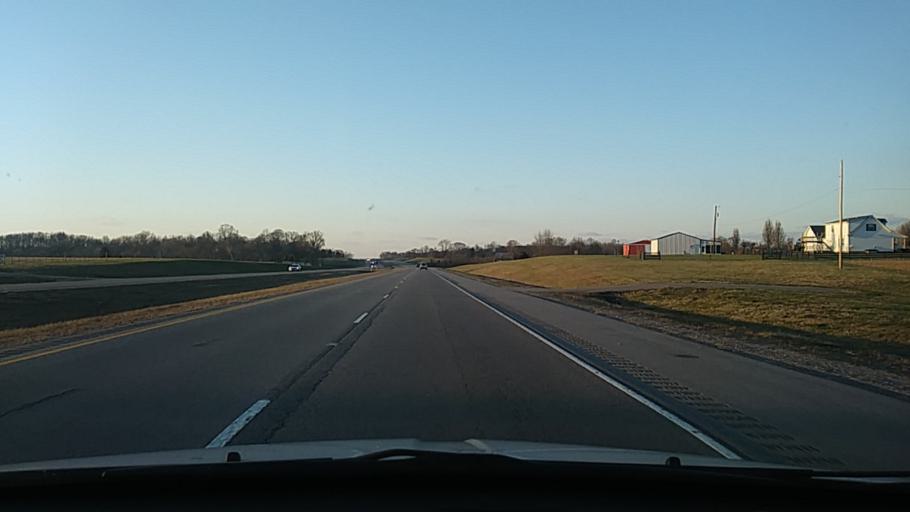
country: US
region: Tennessee
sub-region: Sumner County
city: Portland
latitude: 36.5002
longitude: -86.5006
